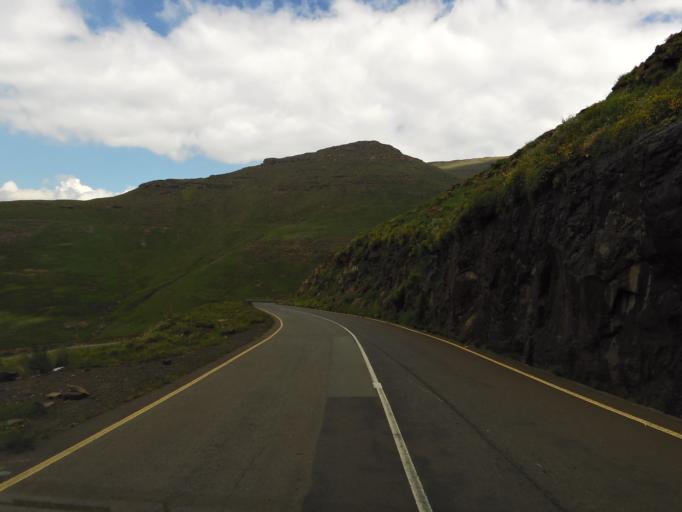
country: LS
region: Butha-Buthe
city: Butha-Buthe
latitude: -29.1151
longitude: 28.4393
